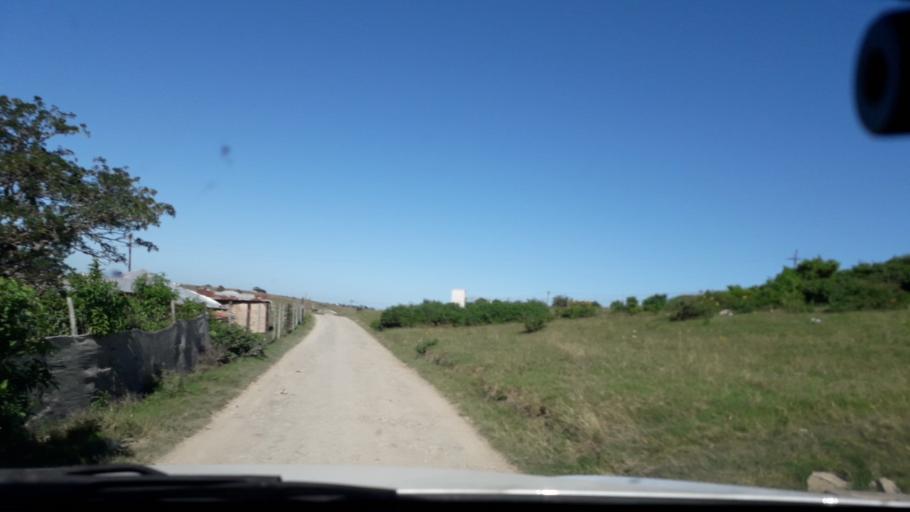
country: ZA
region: Eastern Cape
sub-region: Buffalo City Metropolitan Municipality
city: East London
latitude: -32.8448
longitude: 27.9891
